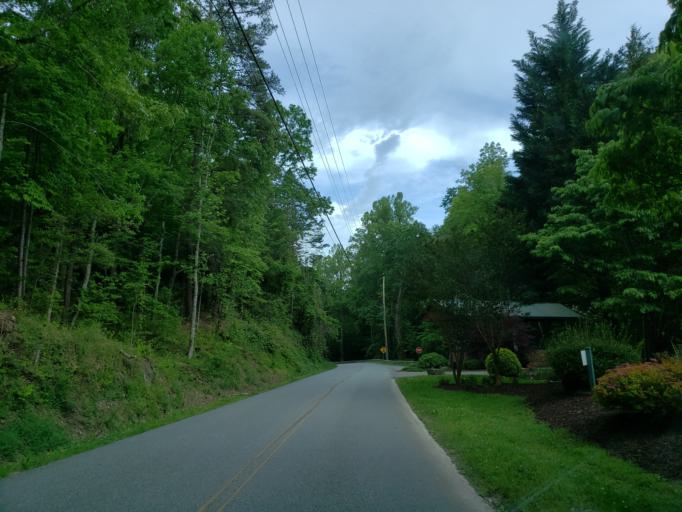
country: US
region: Georgia
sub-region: Fannin County
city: Blue Ridge
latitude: 34.8574
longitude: -84.3392
